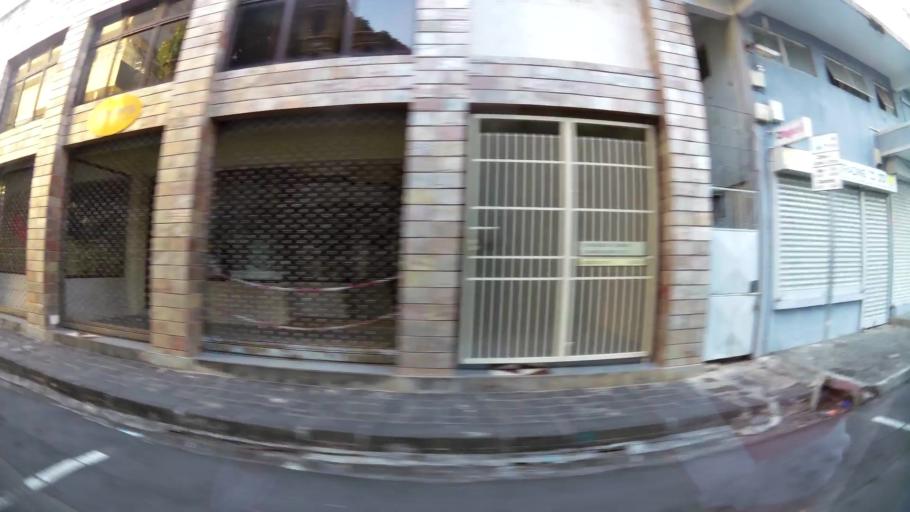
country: MU
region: Port Louis
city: Port Louis
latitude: -20.1669
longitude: 57.4999
